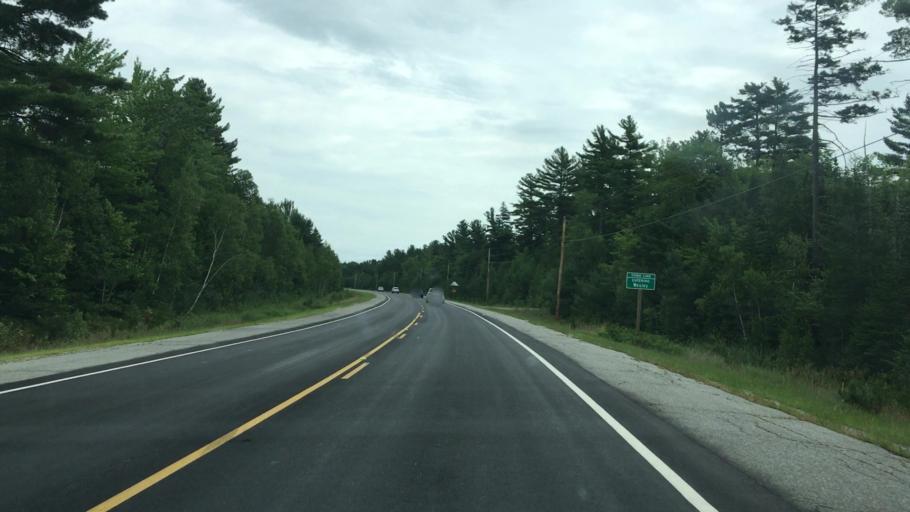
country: US
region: Maine
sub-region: Washington County
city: Addison
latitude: 44.9401
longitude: -67.7205
